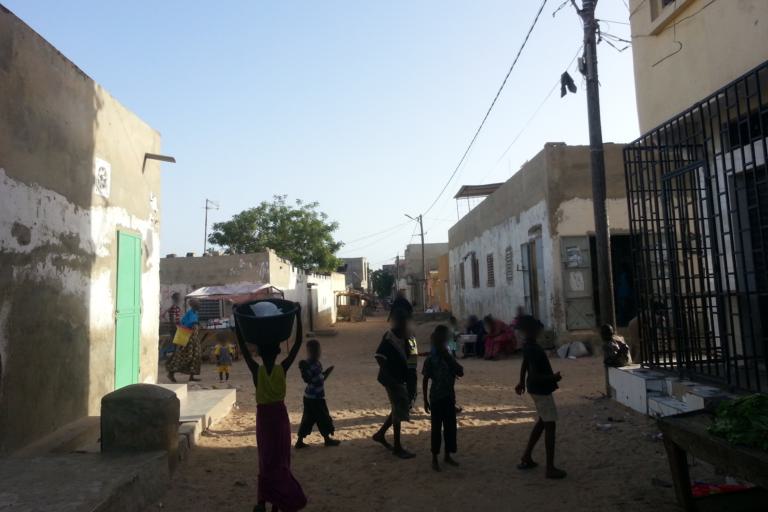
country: SN
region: Dakar
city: Pikine
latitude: 14.7727
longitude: -17.3838
